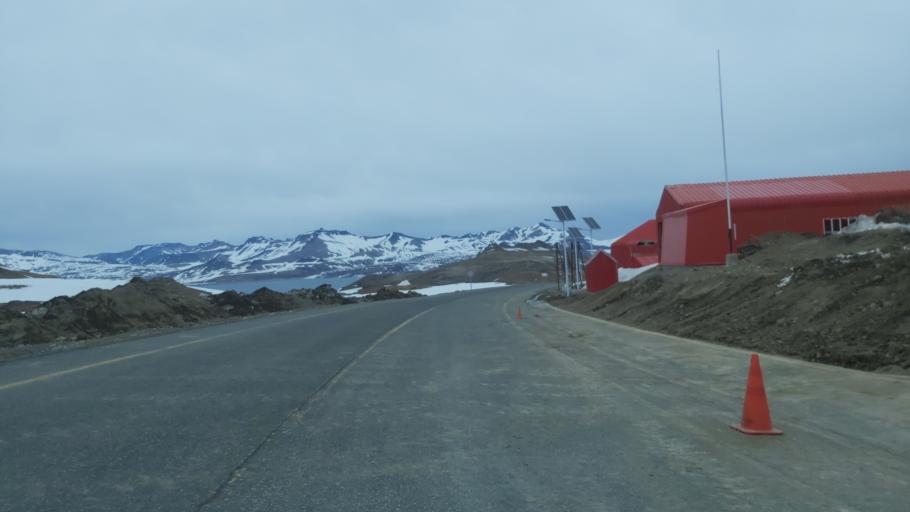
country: CL
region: Maule
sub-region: Provincia de Linares
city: Colbun
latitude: -36.0099
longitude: -70.4824
